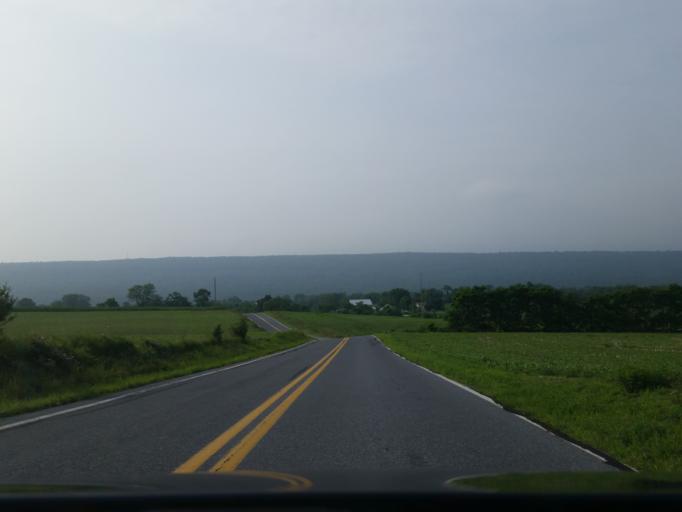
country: US
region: Pennsylvania
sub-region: Lebanon County
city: Palmyra
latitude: 40.3962
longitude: -76.6266
